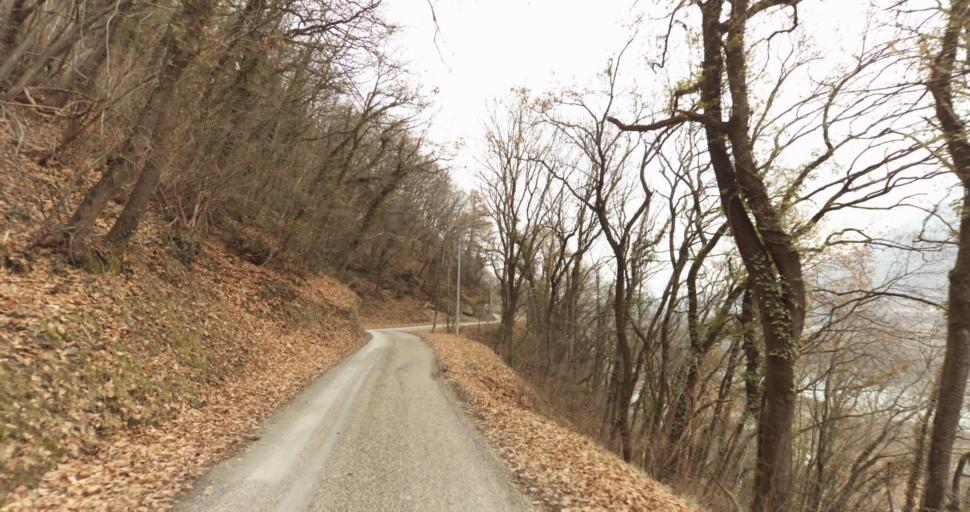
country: FR
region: Rhone-Alpes
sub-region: Departement de l'Isere
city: Saint-Georges-de-Commiers
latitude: 45.0391
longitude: 5.6913
